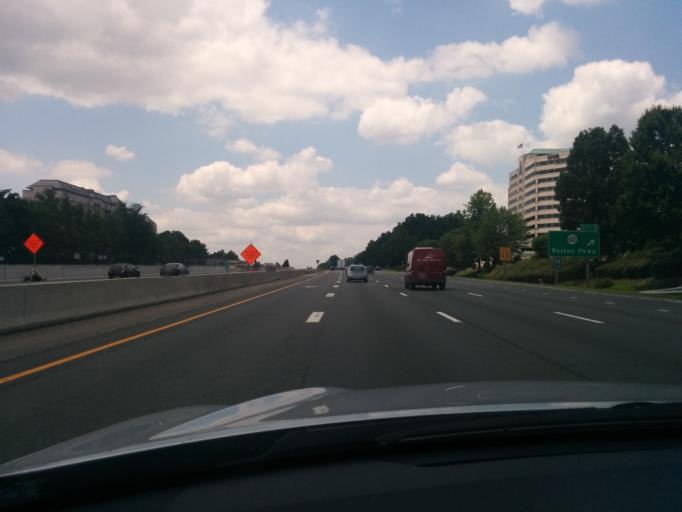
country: US
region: Virginia
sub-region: Fairfax County
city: Reston
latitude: 38.9506
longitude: -77.3478
